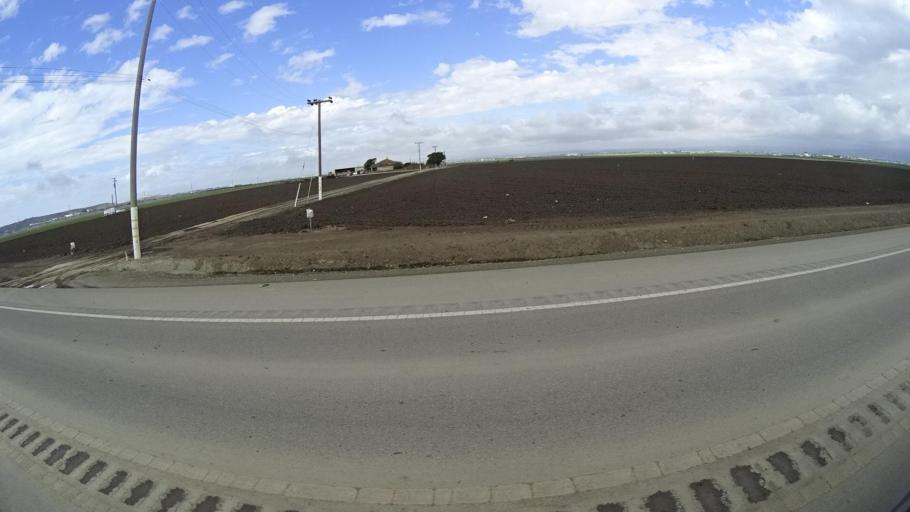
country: US
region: California
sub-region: Monterey County
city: Boronda
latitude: 36.6776
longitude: -121.7227
